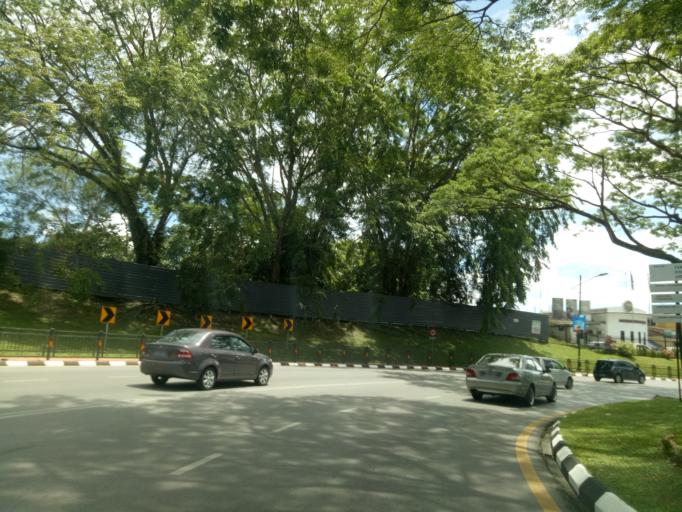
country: MY
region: Sarawak
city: Kuching
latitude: 1.5561
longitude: 110.3430
